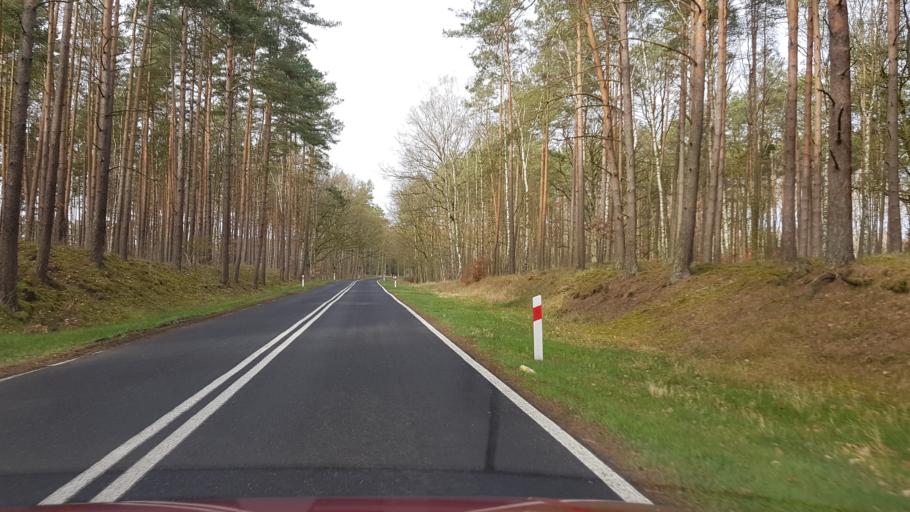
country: PL
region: West Pomeranian Voivodeship
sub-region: Powiat policki
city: Nowe Warpno
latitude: 53.6814
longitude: 14.3559
